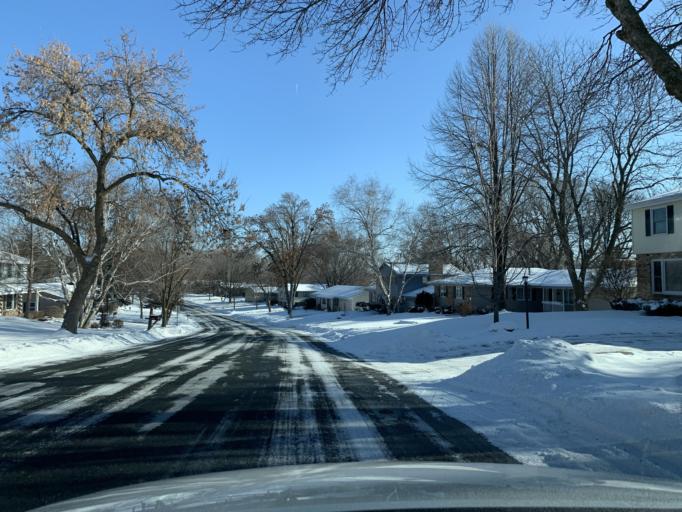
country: US
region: Minnesota
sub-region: Scott County
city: Savage
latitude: 44.8213
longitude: -93.3436
